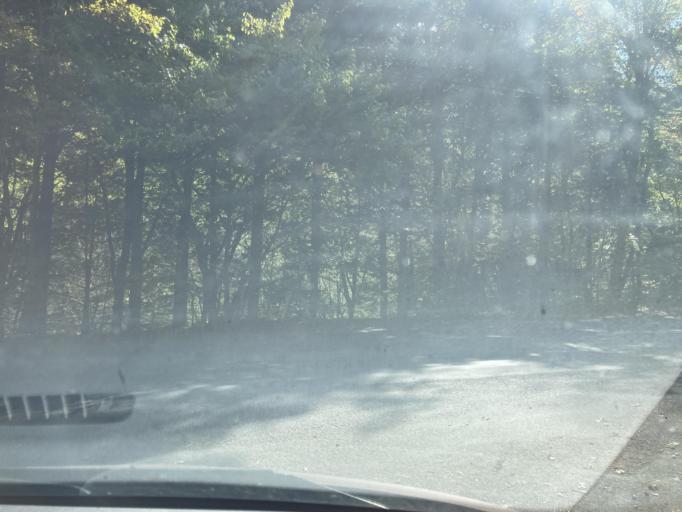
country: JP
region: Nagano
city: Omachi
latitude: 36.4908
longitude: 137.7436
